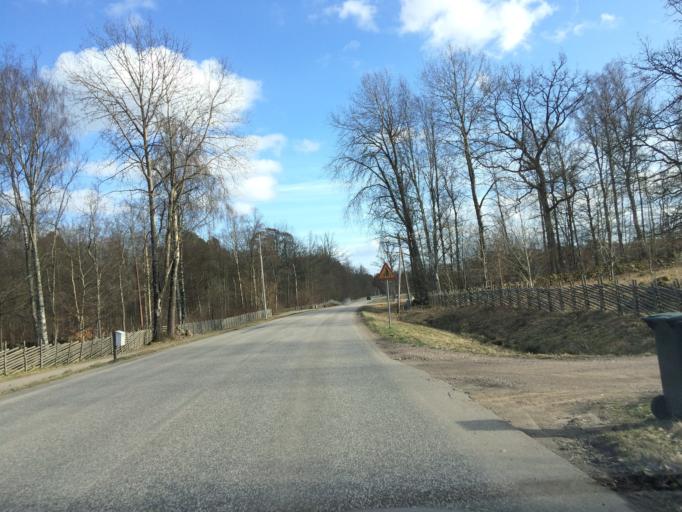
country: SE
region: Kronoberg
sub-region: Almhults Kommun
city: AElmhult
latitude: 56.5658
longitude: 14.1269
